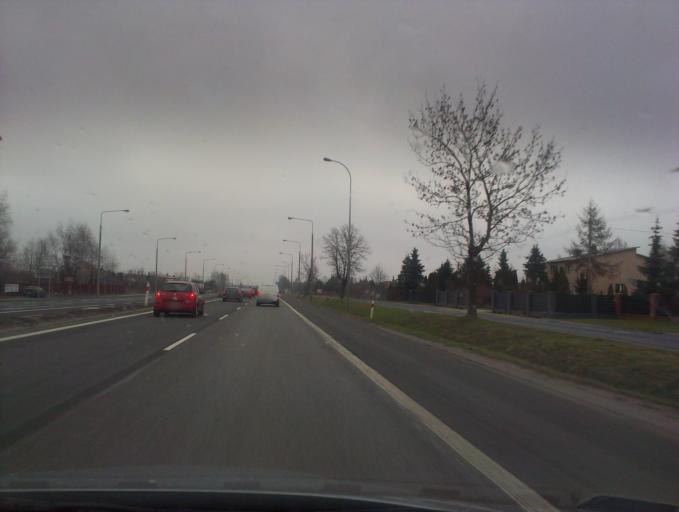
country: PL
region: Masovian Voivodeship
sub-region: Powiat radomski
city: Jedlinsk
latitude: 51.4764
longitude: 21.1310
